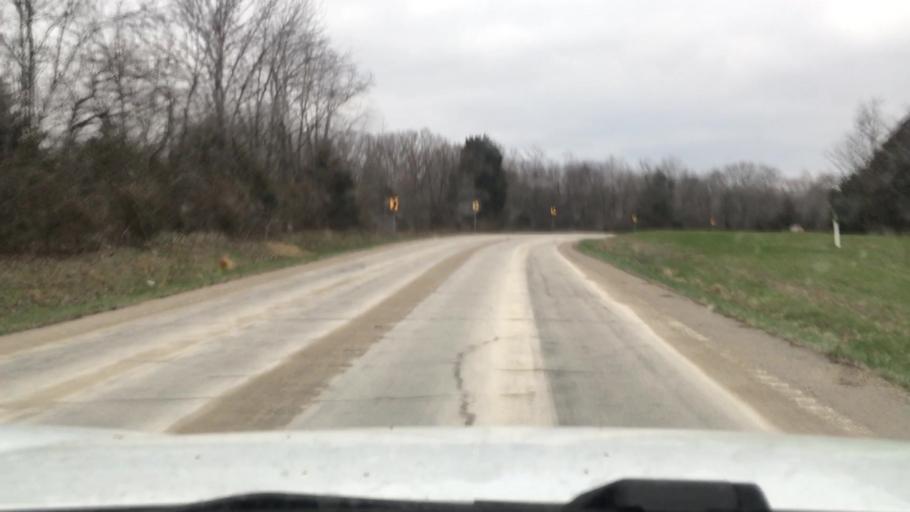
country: US
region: Missouri
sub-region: Saint Charles County
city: Weldon Spring
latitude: 38.6795
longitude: -90.7343
